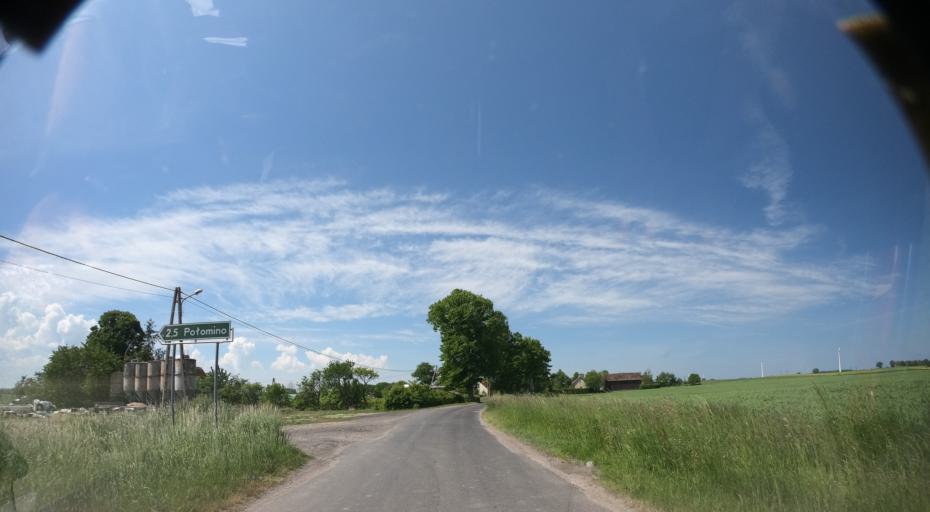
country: PL
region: West Pomeranian Voivodeship
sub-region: Powiat kolobrzeski
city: Dygowo
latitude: 54.1495
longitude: 15.7874
